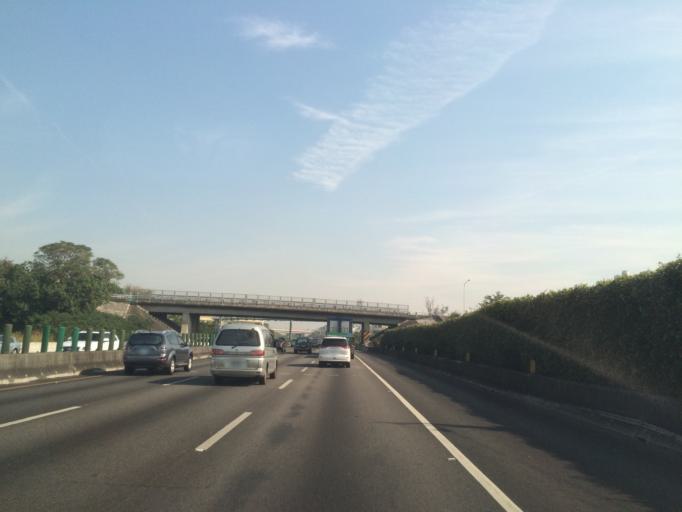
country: TW
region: Taiwan
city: Fengyuan
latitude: 24.2121
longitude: 120.6702
